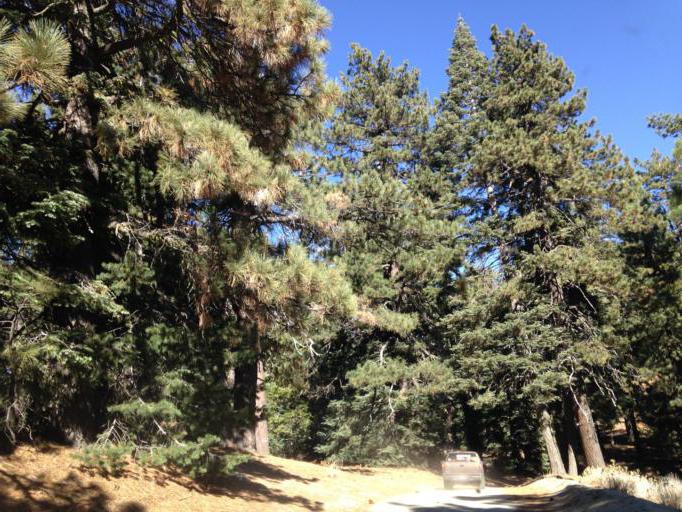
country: US
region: California
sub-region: Riverside County
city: Idyllwild-Pine Cove
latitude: 33.8262
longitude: -116.7511
